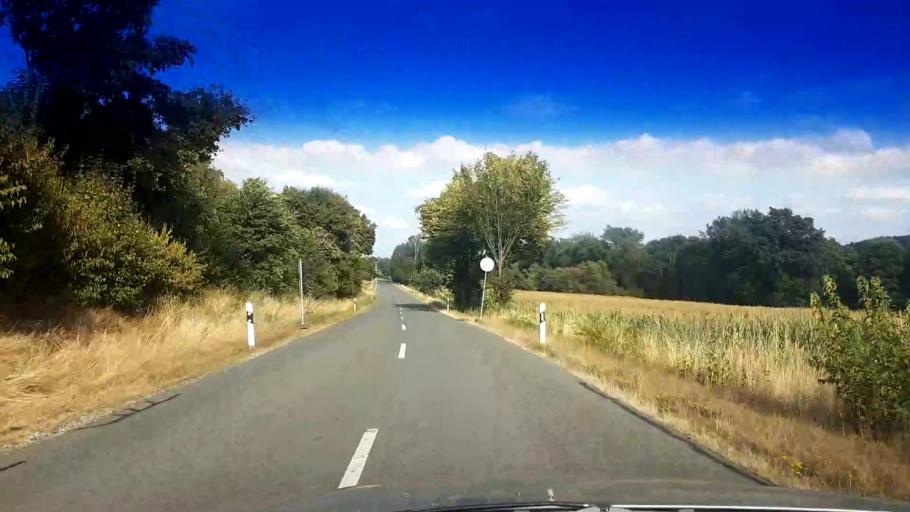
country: DE
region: Bavaria
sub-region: Upper Palatinate
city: Waldsassen
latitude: 50.0239
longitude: 12.3352
